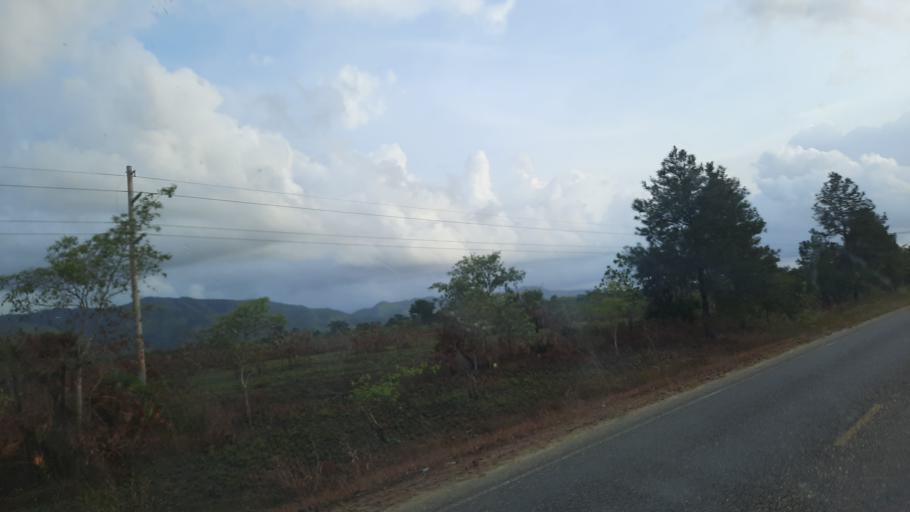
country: BZ
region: Stann Creek
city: Placencia
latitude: 16.6924
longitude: -88.4354
